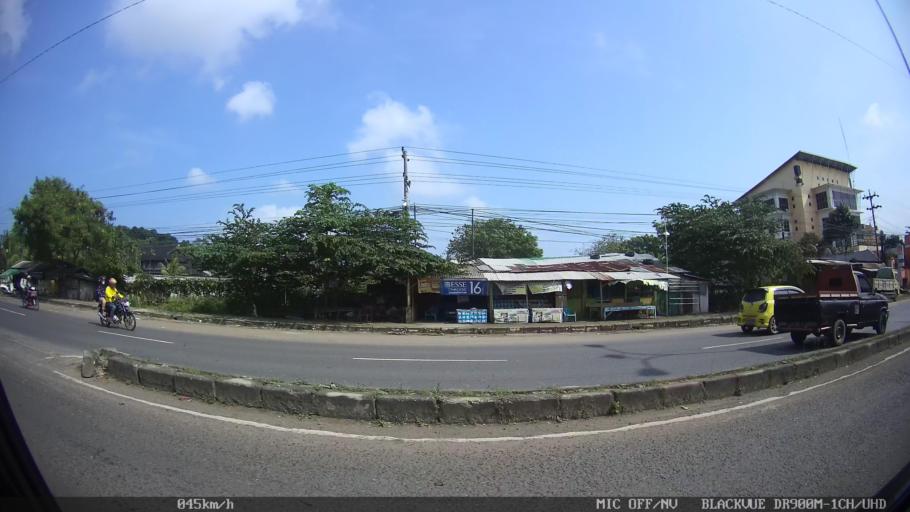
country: ID
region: Lampung
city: Kedaton
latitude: -5.3603
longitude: 105.2288
